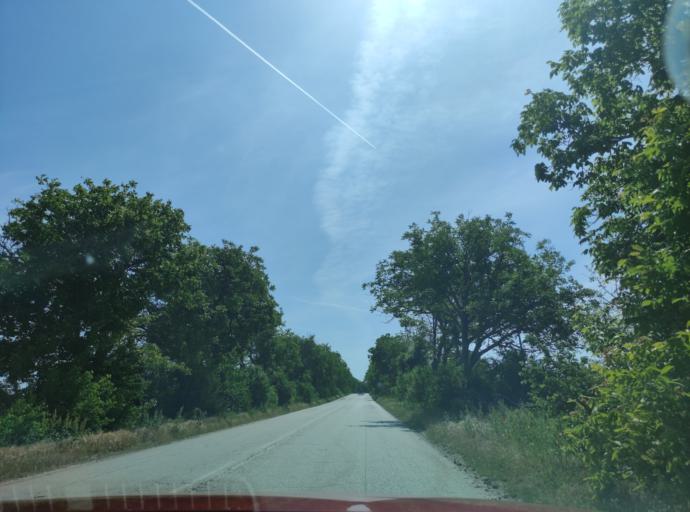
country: BG
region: Pleven
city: Iskur
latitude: 43.4487
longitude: 24.3220
